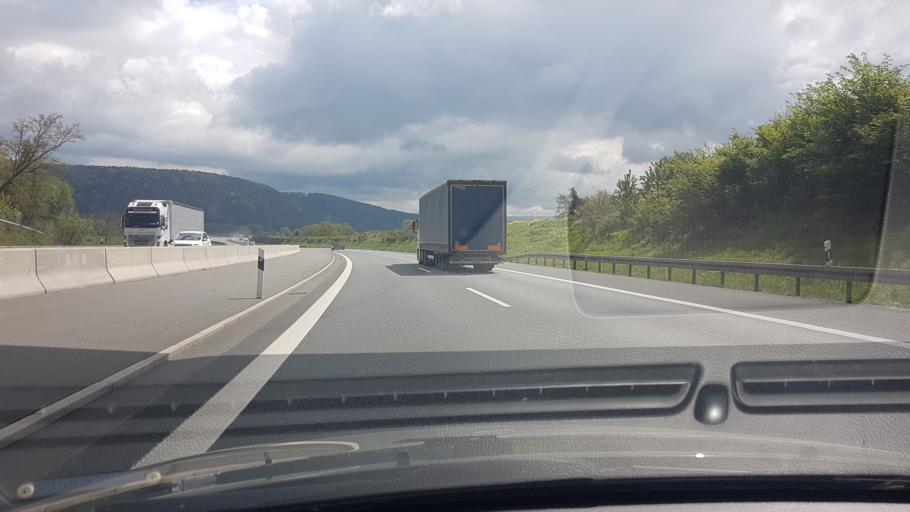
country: DE
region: Bavaria
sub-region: Upper Franconia
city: Neudrossenfeld
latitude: 50.0356
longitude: 11.5230
